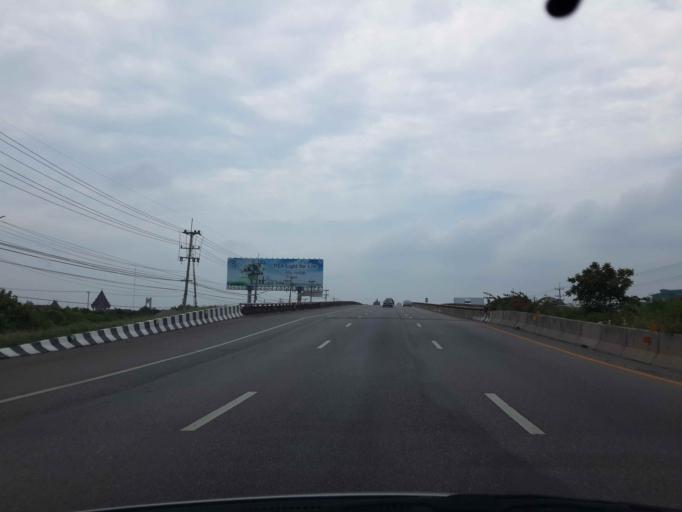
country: TH
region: Samut Sakhon
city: Ban Phaeo
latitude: 13.4882
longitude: 100.1217
